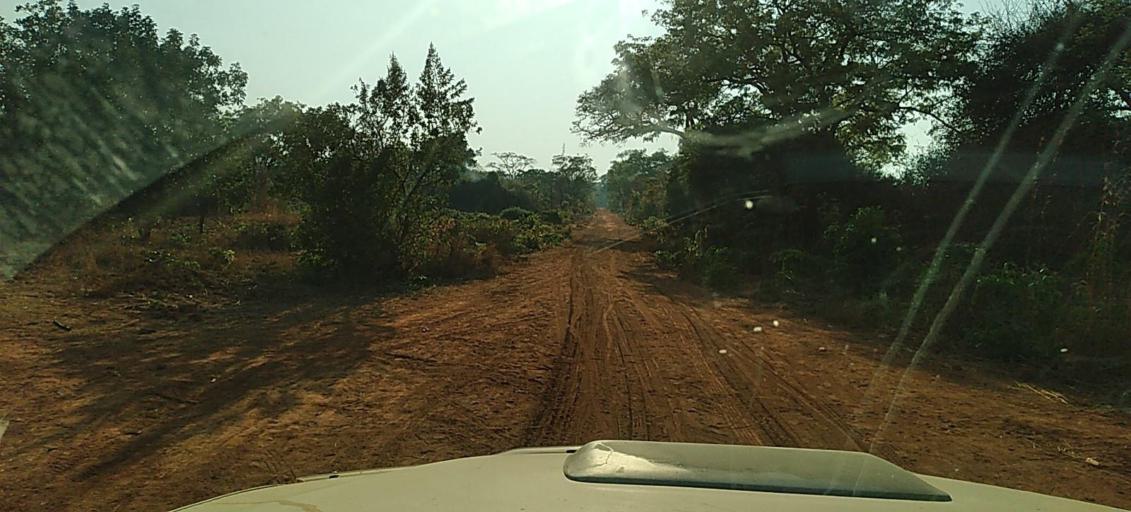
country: ZM
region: North-Western
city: Kasempa
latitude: -13.1675
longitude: 25.8824
